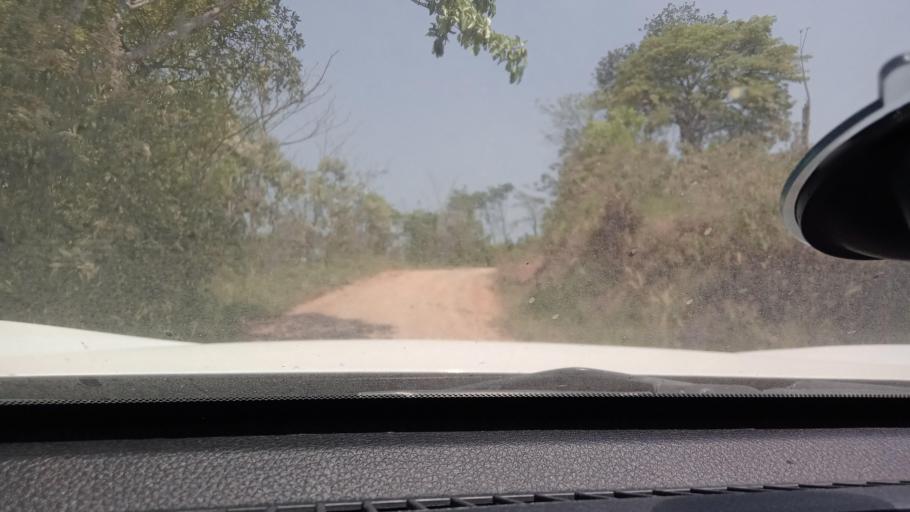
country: MX
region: Tabasco
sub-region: Huimanguillo
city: Francisco Rueda
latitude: 17.4939
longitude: -93.9170
